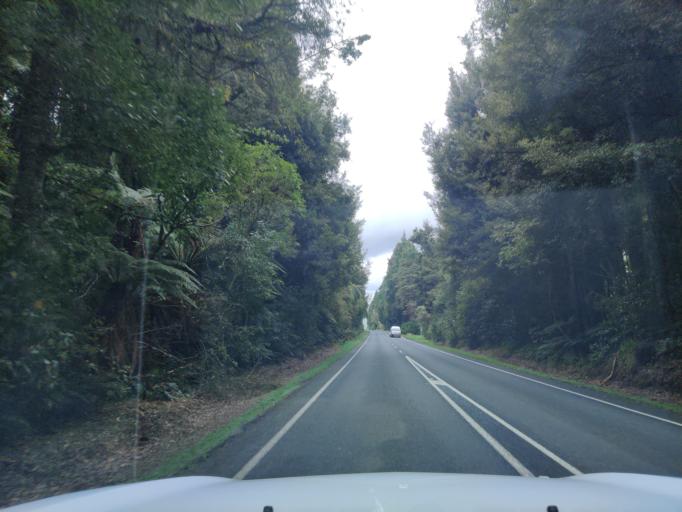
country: NZ
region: Waikato
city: Turangi
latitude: -38.9952
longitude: 175.3783
